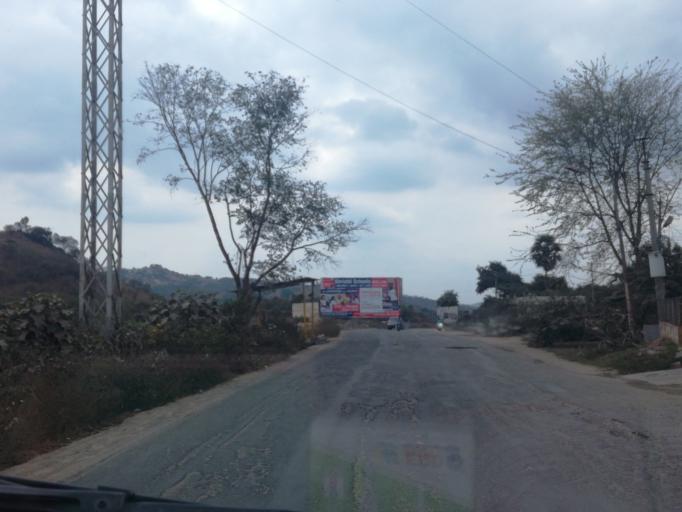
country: IN
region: Andhra Pradesh
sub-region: Chittoor
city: Ramapuram
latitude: 13.0883
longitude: 79.1347
